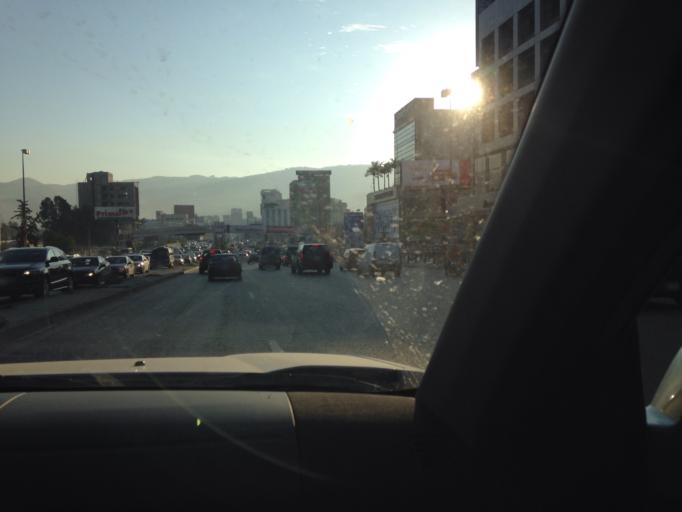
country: LB
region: Mont-Liban
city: Jdaidet el Matn
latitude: 33.8967
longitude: 35.5387
